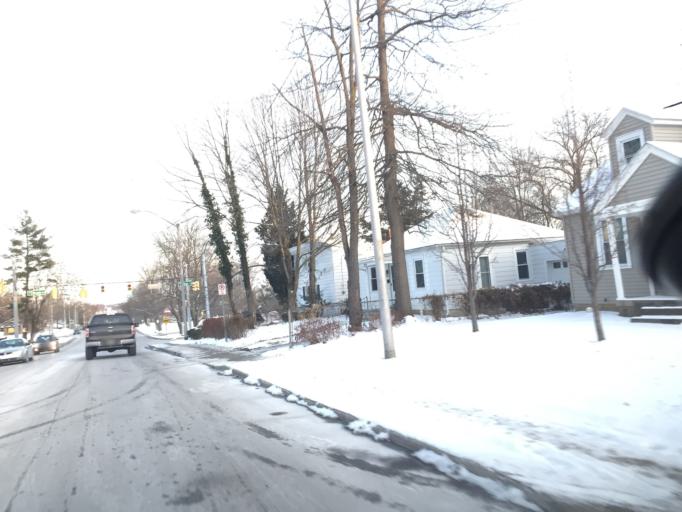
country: US
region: Indiana
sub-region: Monroe County
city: Bloomington
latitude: 39.1643
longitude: -86.5091
